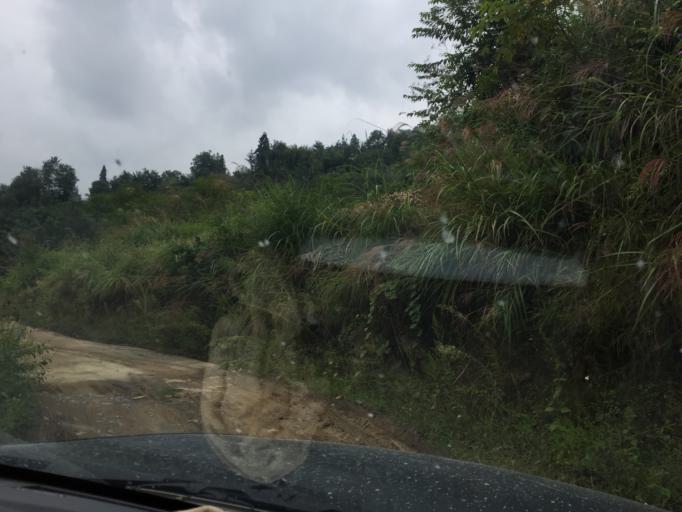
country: CN
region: Guizhou Sheng
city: Nangan
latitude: 28.2517
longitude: 107.9456
